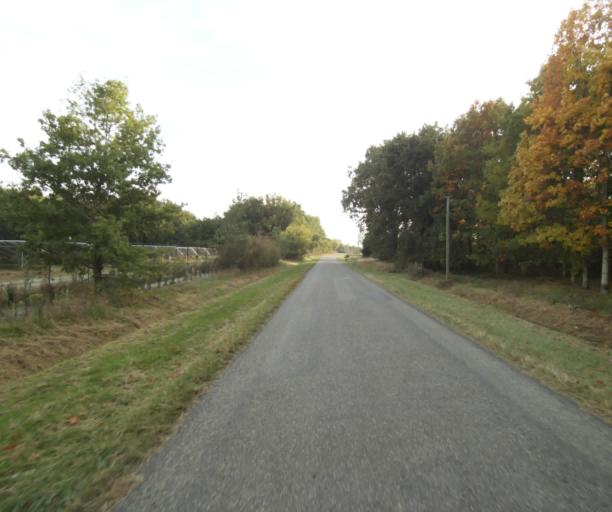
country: FR
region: Midi-Pyrenees
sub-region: Departement du Tarn-et-Garonne
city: Campsas
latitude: 43.8794
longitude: 1.3209
